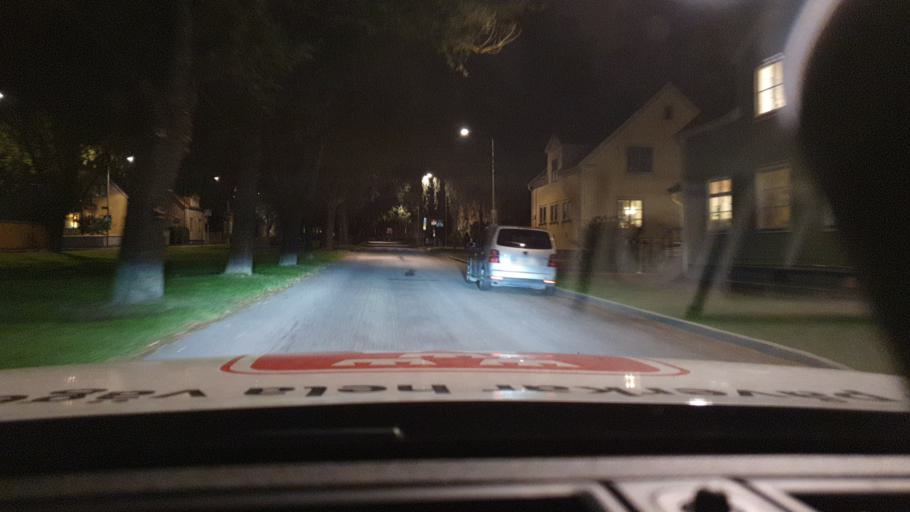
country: SE
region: Stockholm
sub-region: Stockholms Kommun
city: Arsta
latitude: 59.2797
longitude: 18.0856
